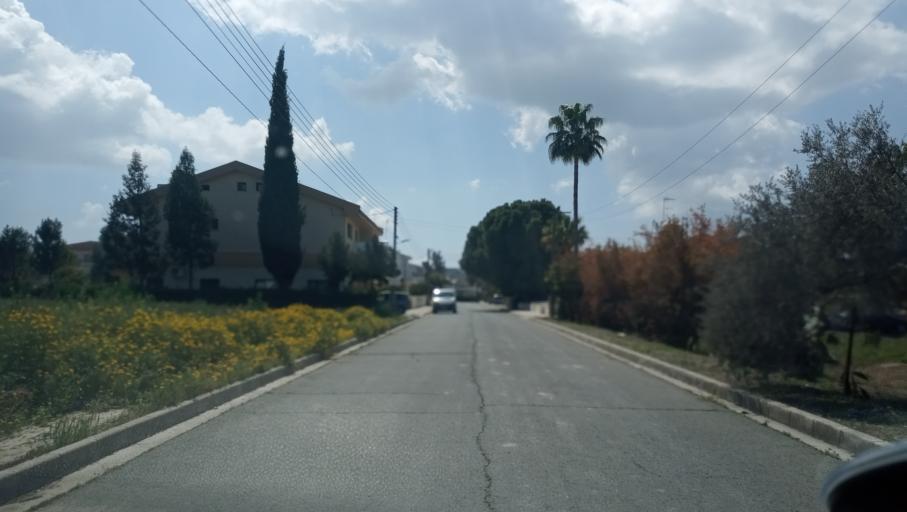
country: CY
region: Lefkosia
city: Dali
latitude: 35.0198
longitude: 33.4136
